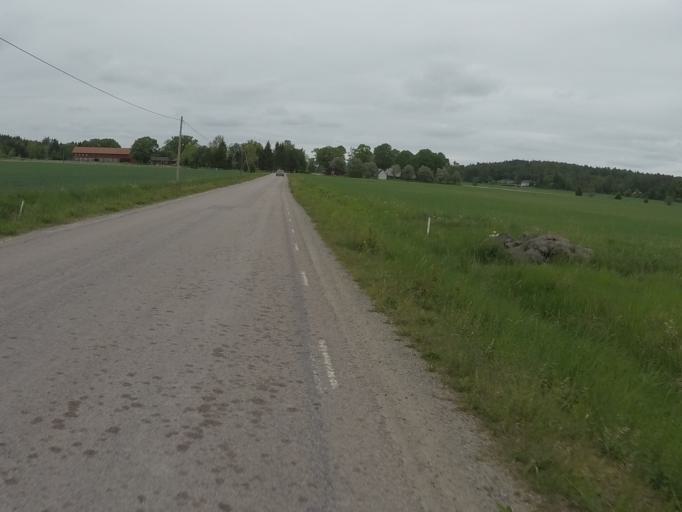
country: SE
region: Vaestmanland
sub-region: Hallstahammars Kommun
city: Kolback
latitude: 59.5449
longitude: 16.3109
